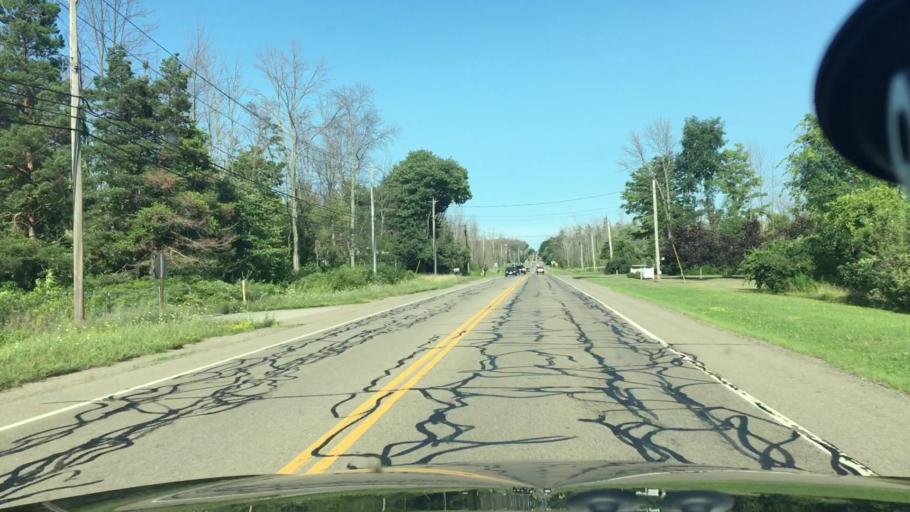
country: US
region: New York
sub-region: Erie County
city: Angola
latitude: 42.6525
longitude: -78.9887
